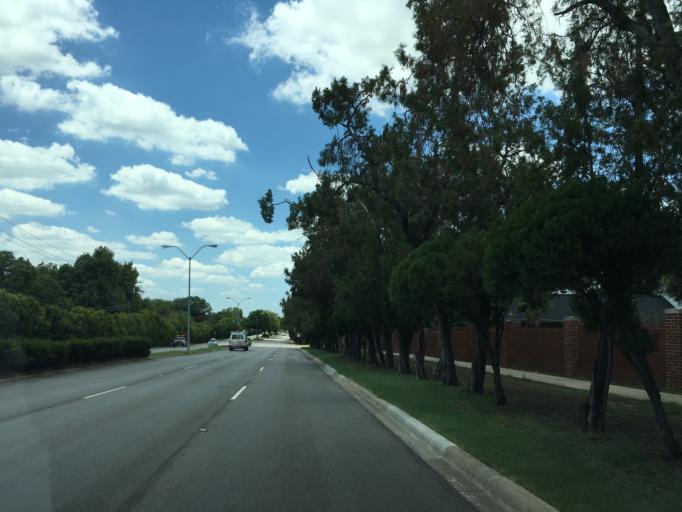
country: US
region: Texas
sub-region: Dallas County
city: Farmers Branch
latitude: 32.9243
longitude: -96.8588
